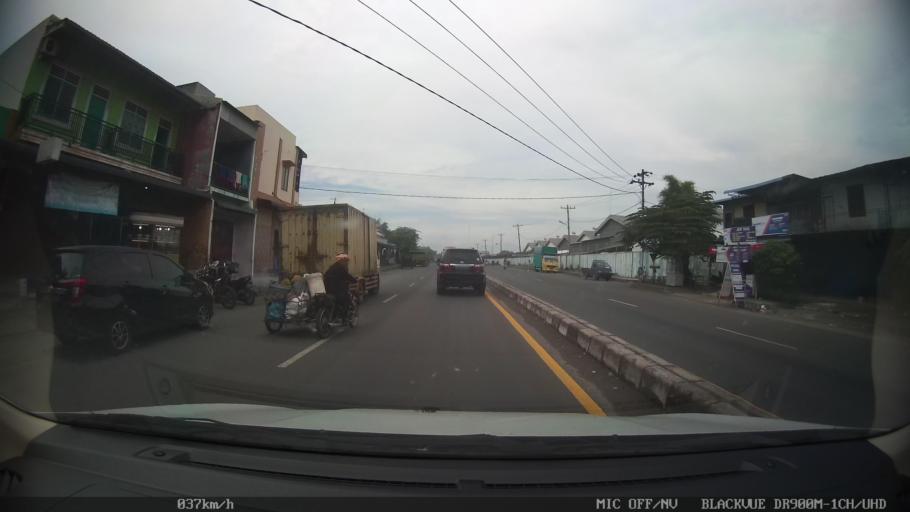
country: ID
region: North Sumatra
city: Sunggal
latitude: 3.6046
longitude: 98.5753
